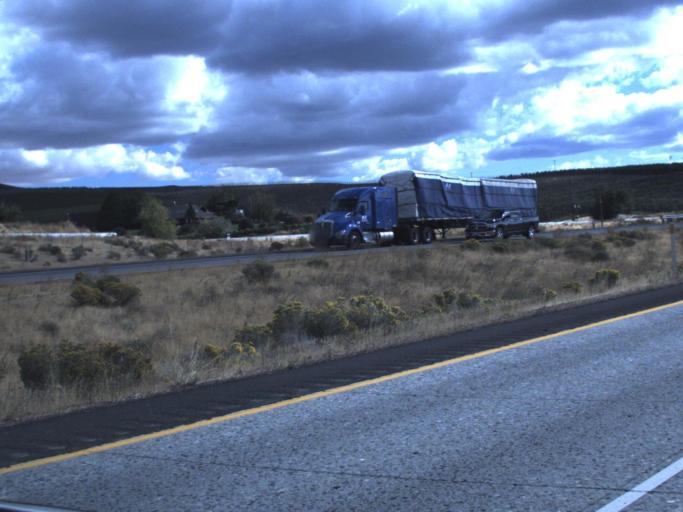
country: US
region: Washington
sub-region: Yakima County
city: Union Gap
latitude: 46.5134
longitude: -120.4538
